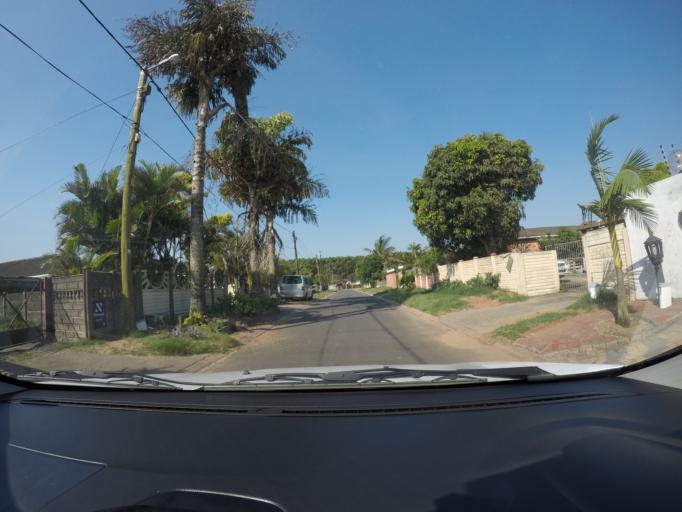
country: ZA
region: KwaZulu-Natal
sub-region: uThungulu District Municipality
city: Richards Bay
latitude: -28.7153
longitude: 32.0422
